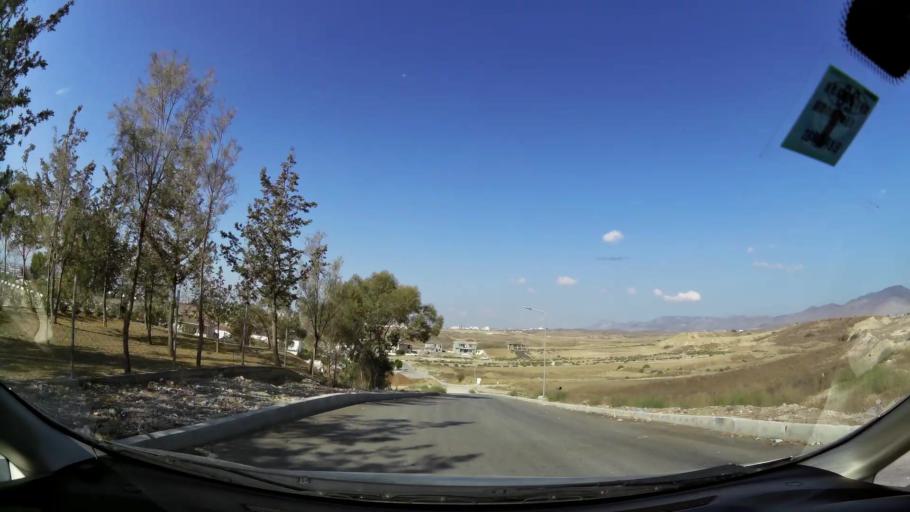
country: CY
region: Lefkosia
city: Nicosia
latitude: 35.2177
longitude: 33.3716
